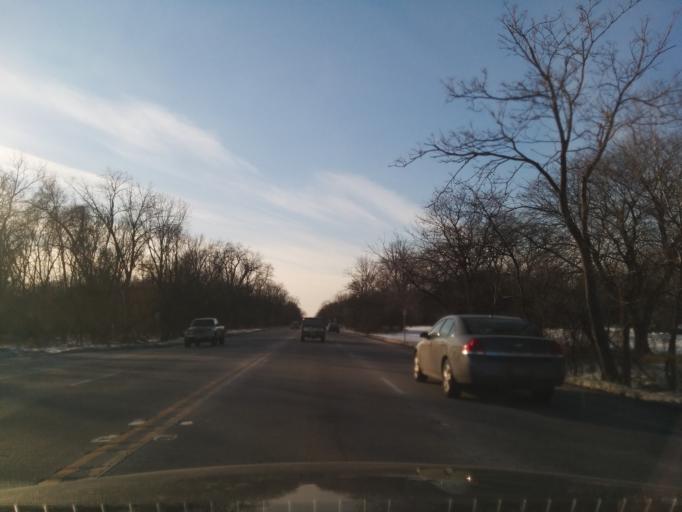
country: US
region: Illinois
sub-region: Cook County
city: Norridge
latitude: 41.9525
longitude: -87.8437
